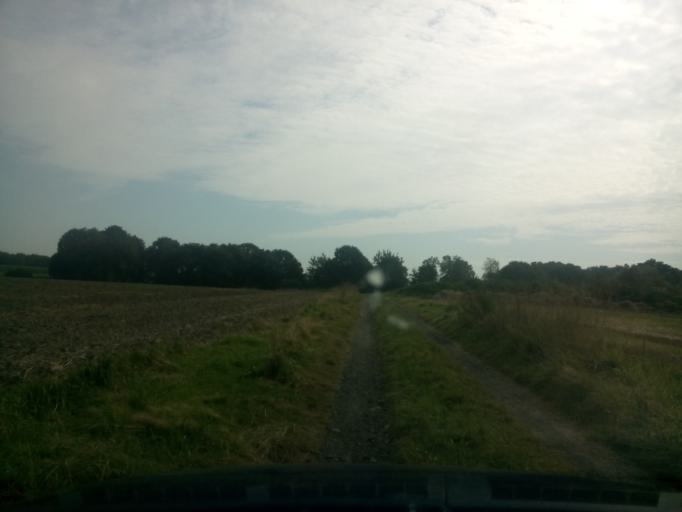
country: DE
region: Lower Saxony
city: Osterholz-Scharmbeck
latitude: 53.2374
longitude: 8.7698
